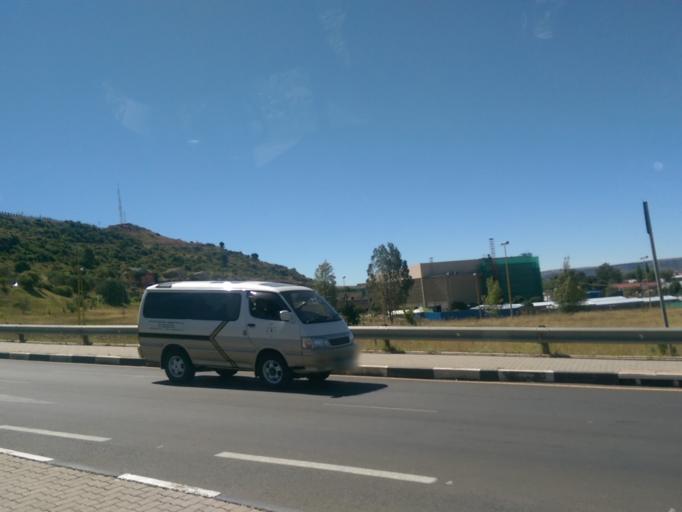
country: LS
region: Maseru
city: Maseru
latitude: -29.3256
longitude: 27.4991
